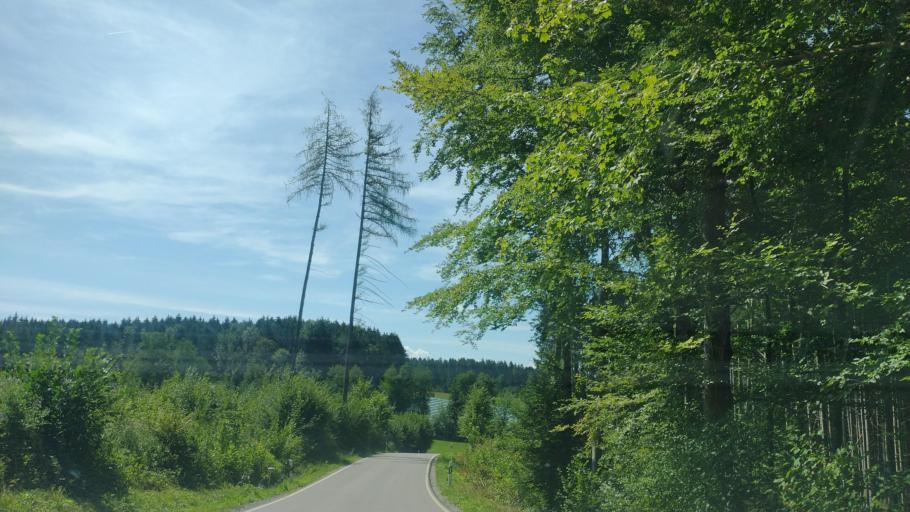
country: DE
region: Baden-Wuerttemberg
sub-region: Tuebingen Region
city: Neukirch
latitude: 47.6540
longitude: 9.6489
